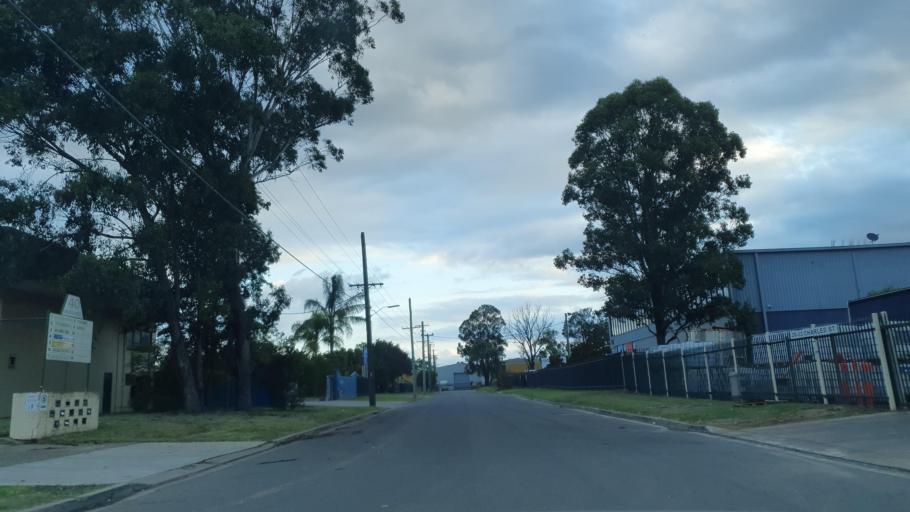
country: AU
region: New South Wales
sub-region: Penrith Municipality
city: Werrington County
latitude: -33.7434
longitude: 150.7689
